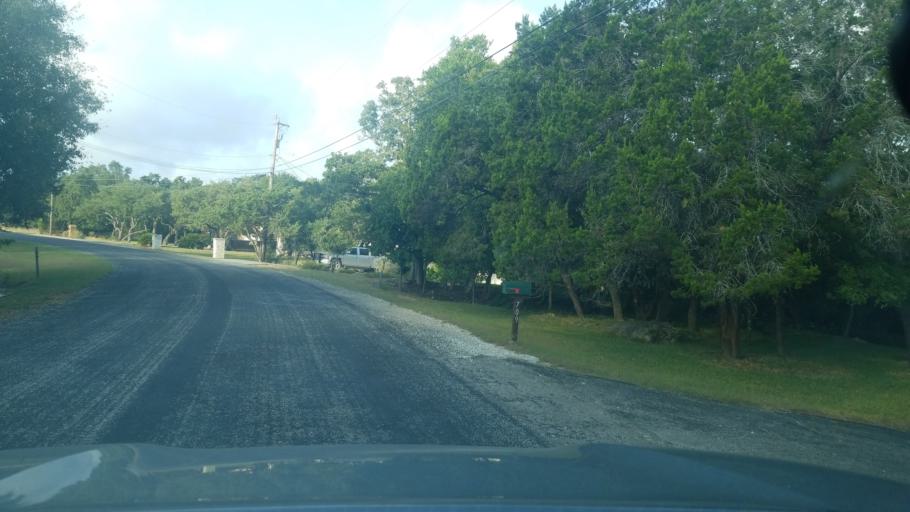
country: US
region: Texas
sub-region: Bexar County
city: Timberwood Park
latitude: 29.7016
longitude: -98.5051
